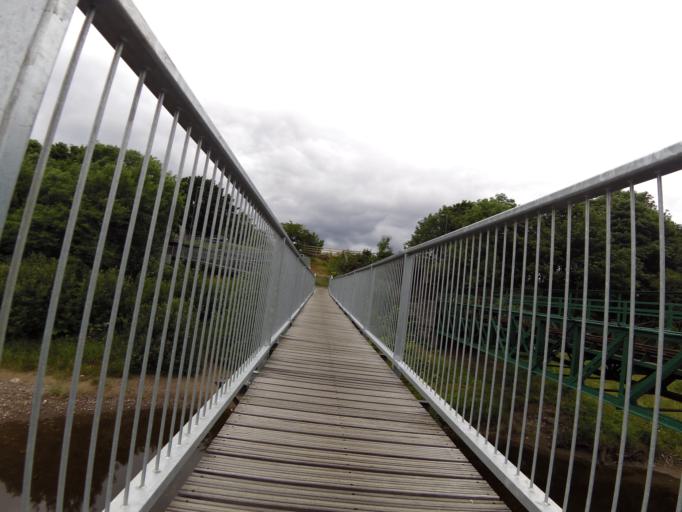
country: GB
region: Scotland
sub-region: Highland
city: Fort William
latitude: 56.8333
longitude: -5.0840
